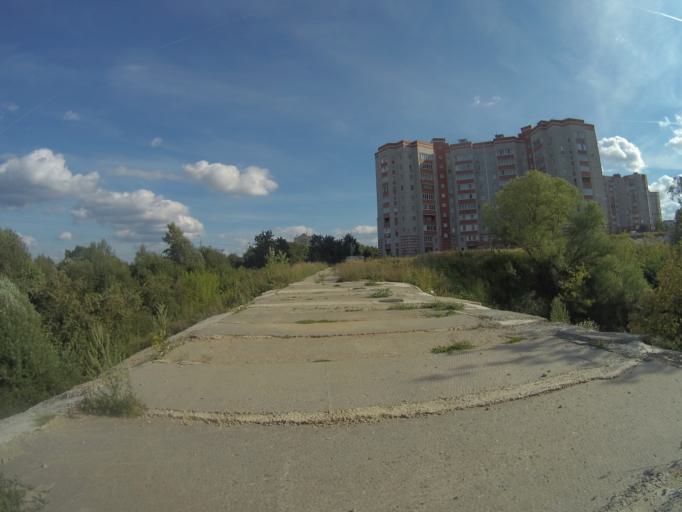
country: RU
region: Vladimir
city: Vladimir
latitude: 56.1380
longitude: 40.3776
